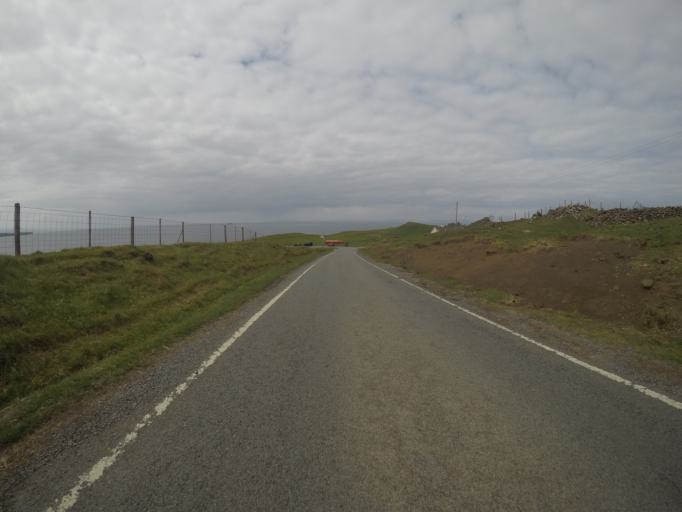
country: GB
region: Scotland
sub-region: Highland
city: Portree
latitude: 57.6817
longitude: -6.3426
